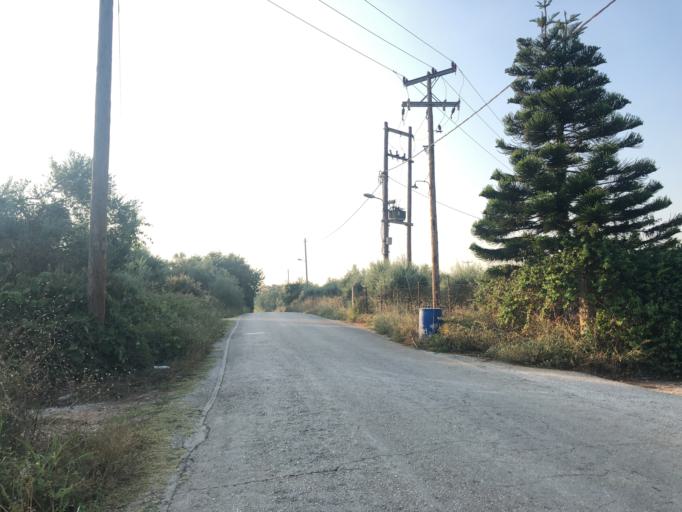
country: GR
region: Crete
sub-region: Nomos Chanias
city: Georgioupolis
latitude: 35.3511
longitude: 24.2769
